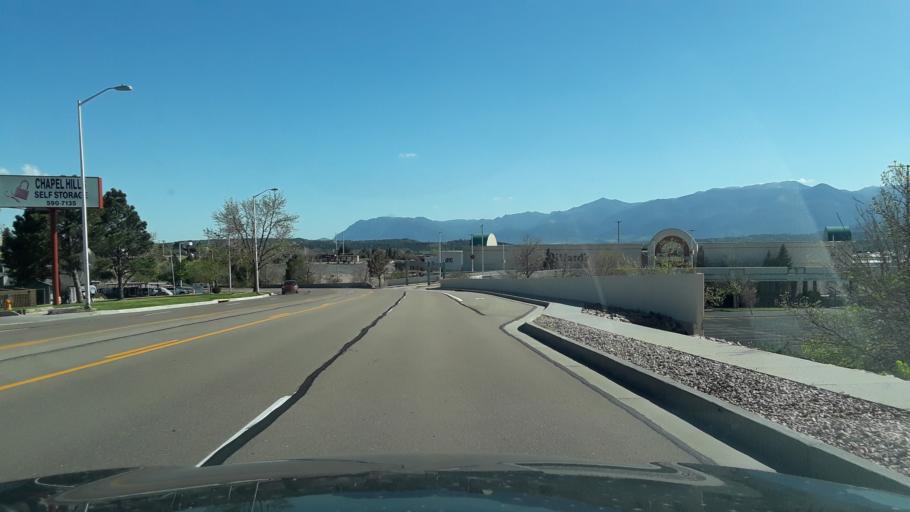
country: US
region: Colorado
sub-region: El Paso County
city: Air Force Academy
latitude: 38.9505
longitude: -104.7919
